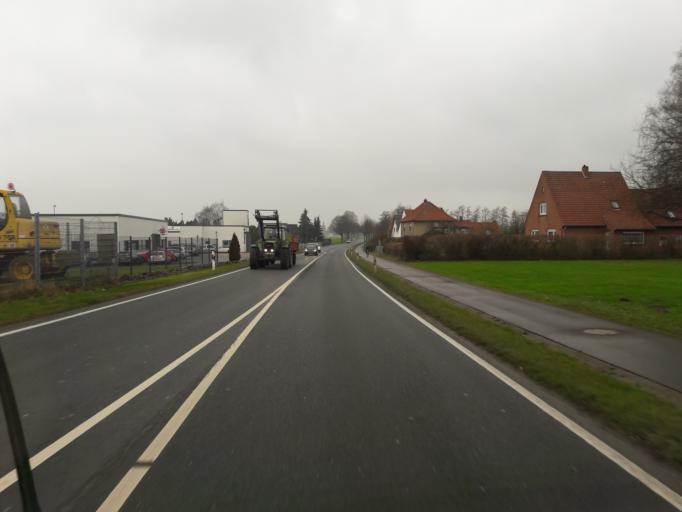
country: DE
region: North Rhine-Westphalia
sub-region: Regierungsbezirk Detmold
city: Minden
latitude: 52.3092
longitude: 8.8401
